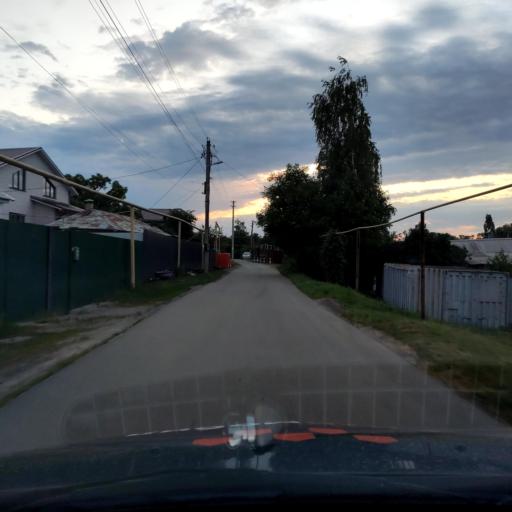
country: RU
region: Voronezj
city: Shilovo
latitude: 51.4540
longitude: 39.0285
